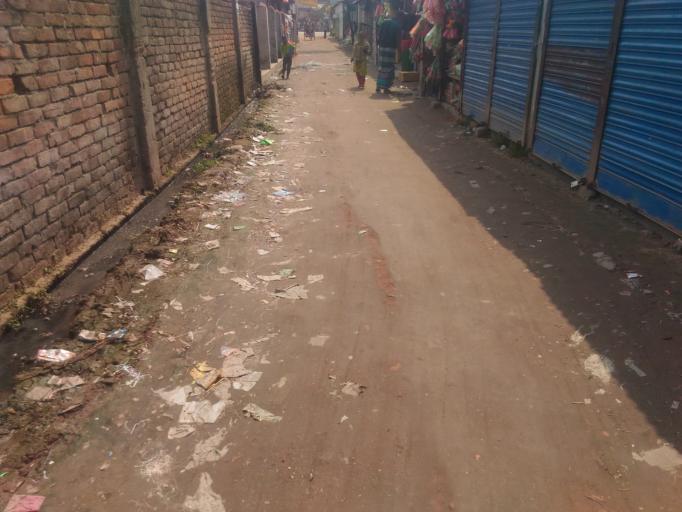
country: BD
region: Dhaka
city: Tungi
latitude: 23.9905
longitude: 90.3756
